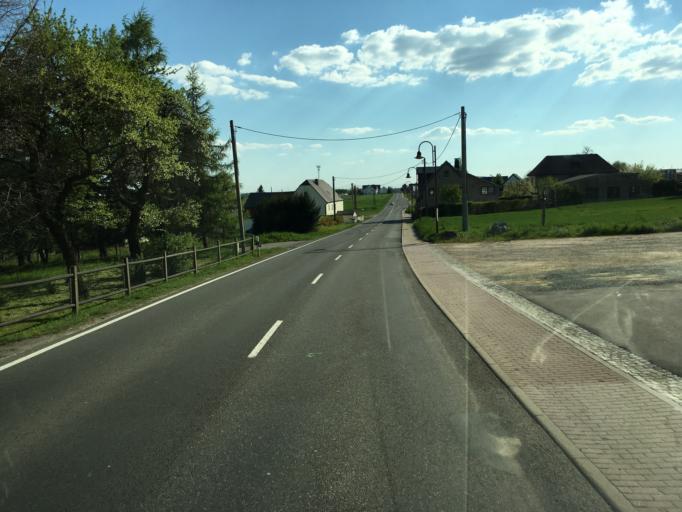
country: DE
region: Saxony
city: Hainichen
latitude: 51.0013
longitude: 13.1269
